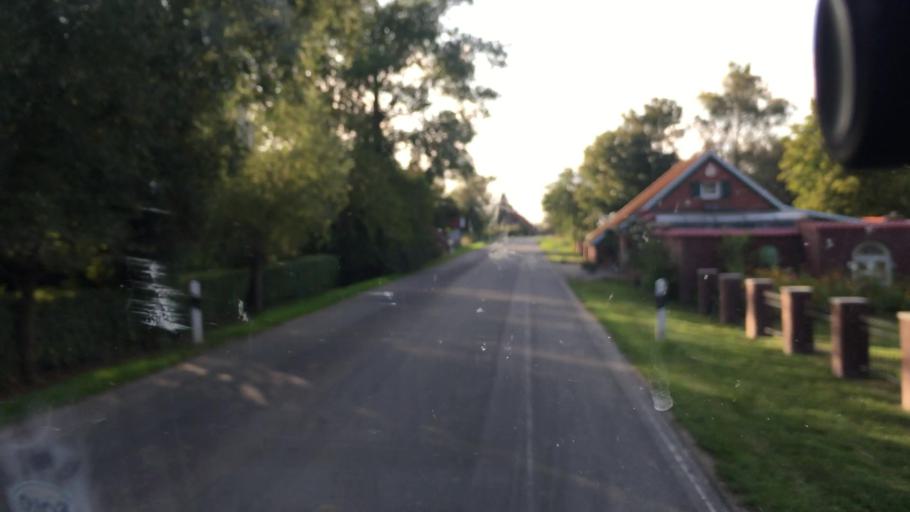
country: DE
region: Lower Saxony
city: Werdum
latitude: 53.6552
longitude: 7.7790
